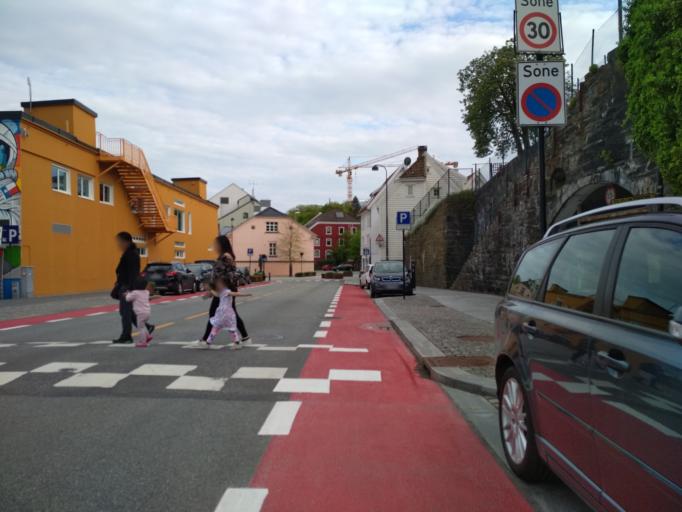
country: NO
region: Rogaland
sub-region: Stavanger
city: Stavanger
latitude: 58.9729
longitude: 5.7261
